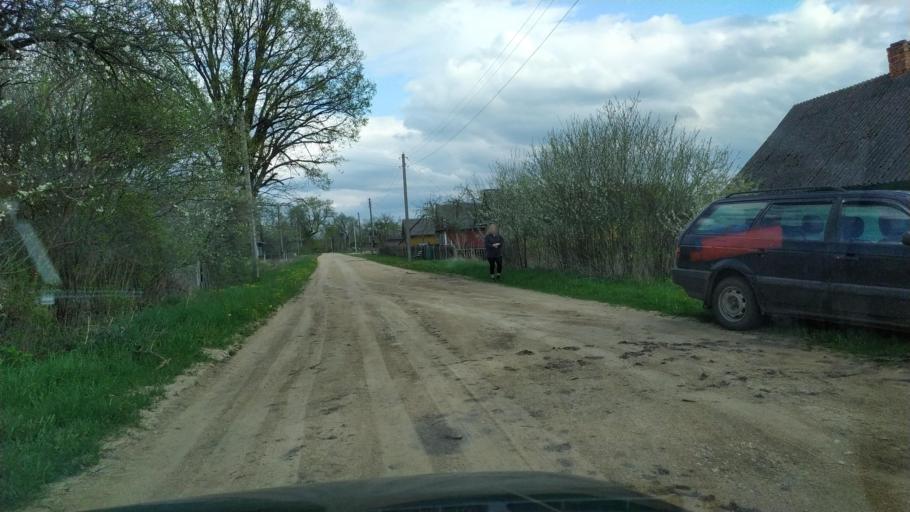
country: BY
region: Brest
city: Pruzhany
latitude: 52.7069
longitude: 24.2597
